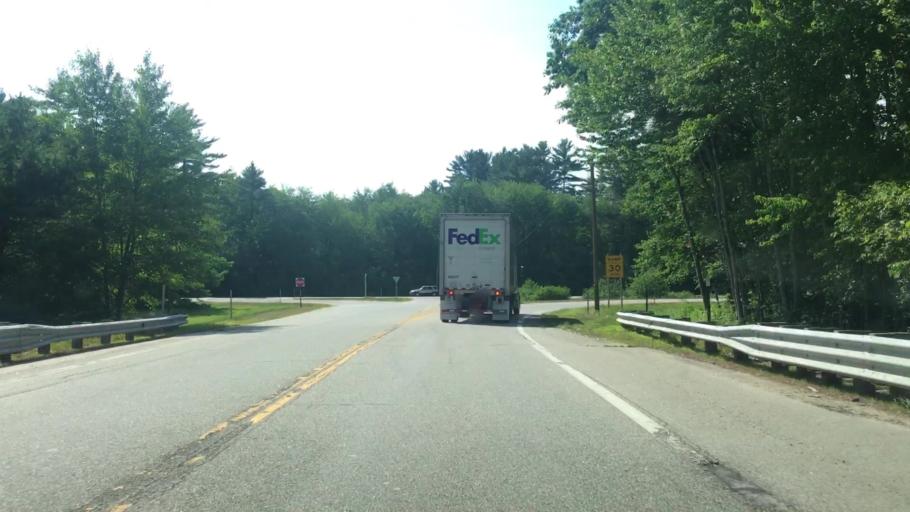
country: US
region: New Hampshire
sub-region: Strafford County
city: Rochester
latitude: 43.3312
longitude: -70.9733
